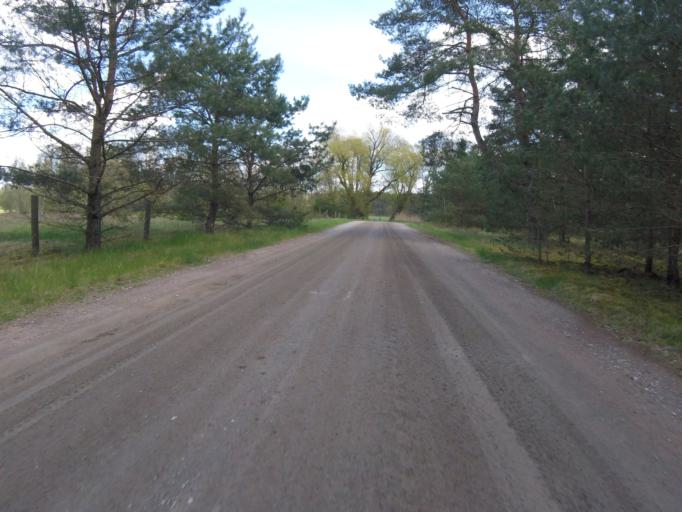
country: DE
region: Brandenburg
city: Munchehofe
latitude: 52.2129
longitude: 13.7740
